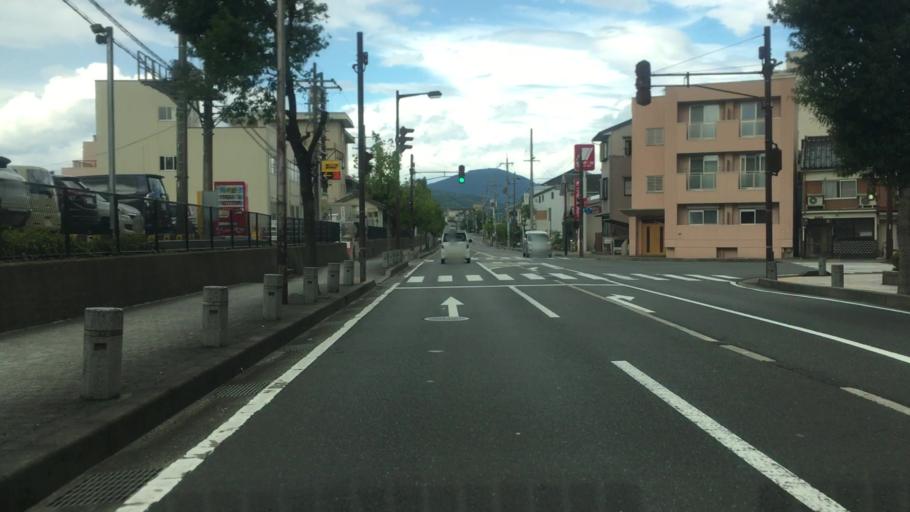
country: JP
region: Hyogo
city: Toyooka
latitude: 35.5446
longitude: 134.8141
